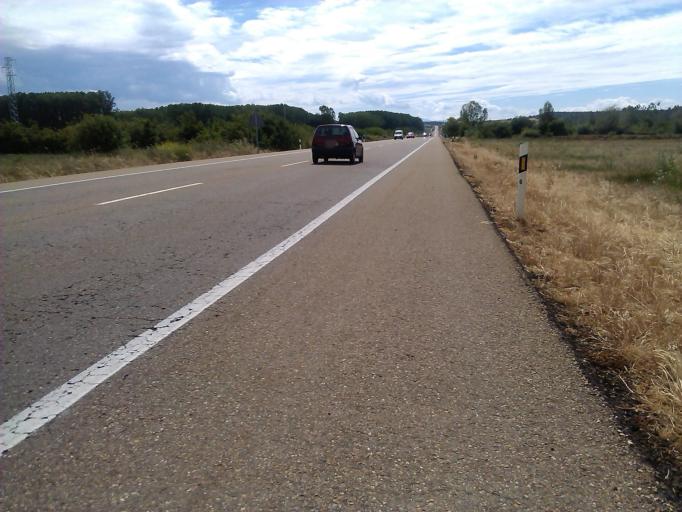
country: ES
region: Castille and Leon
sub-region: Provincia de Leon
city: Villarejo de Orbigo
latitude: 42.4558
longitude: -5.8992
